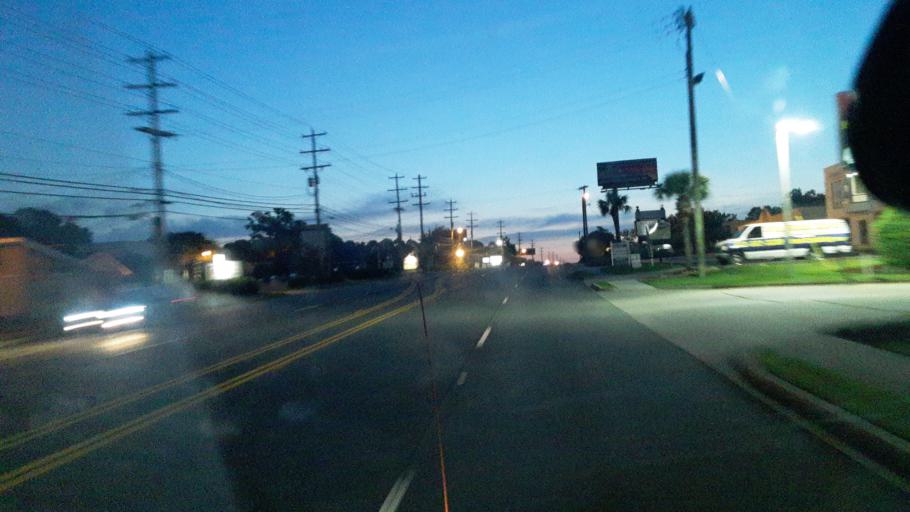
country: US
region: South Carolina
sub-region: Horry County
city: Little River
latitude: 33.8744
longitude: -78.6191
